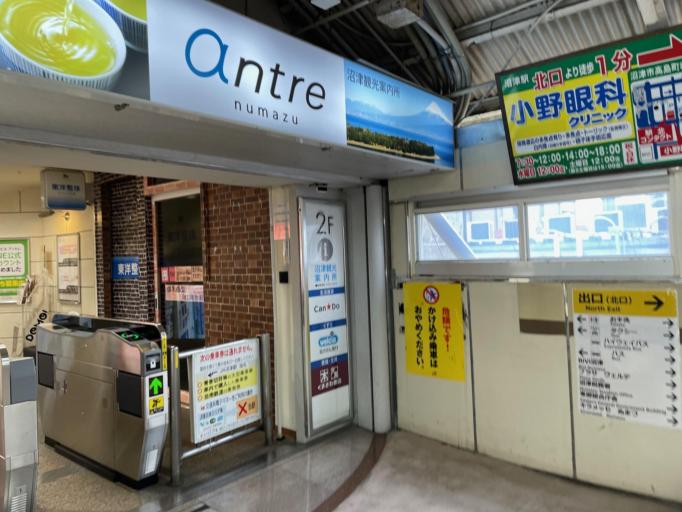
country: JP
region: Shizuoka
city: Numazu
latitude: 35.1027
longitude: 138.8594
